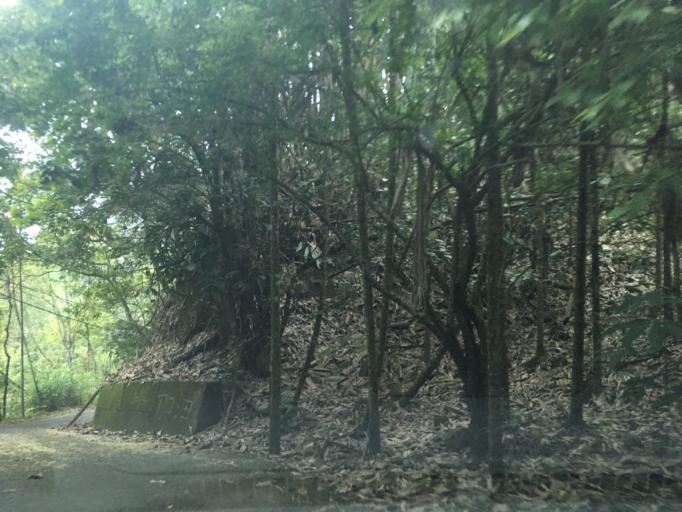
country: TW
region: Taiwan
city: Zhongxing New Village
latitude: 24.0481
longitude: 120.8060
